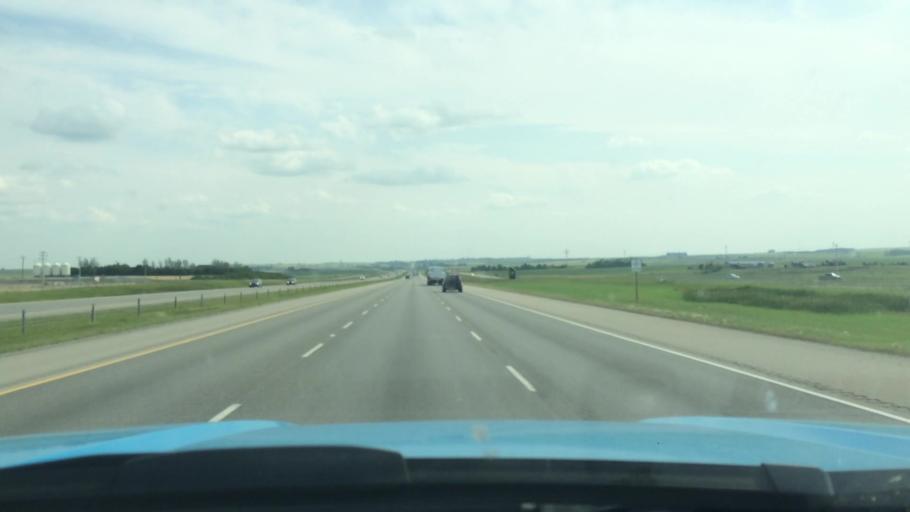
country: CA
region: Alberta
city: Crossfield
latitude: 51.4920
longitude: -114.0253
